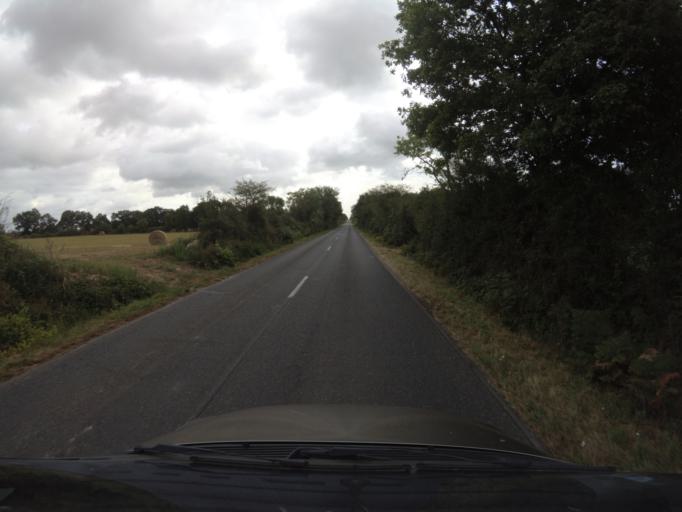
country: FR
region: Pays de la Loire
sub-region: Departement de la Loire-Atlantique
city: Getigne
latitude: 47.0782
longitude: -1.2265
